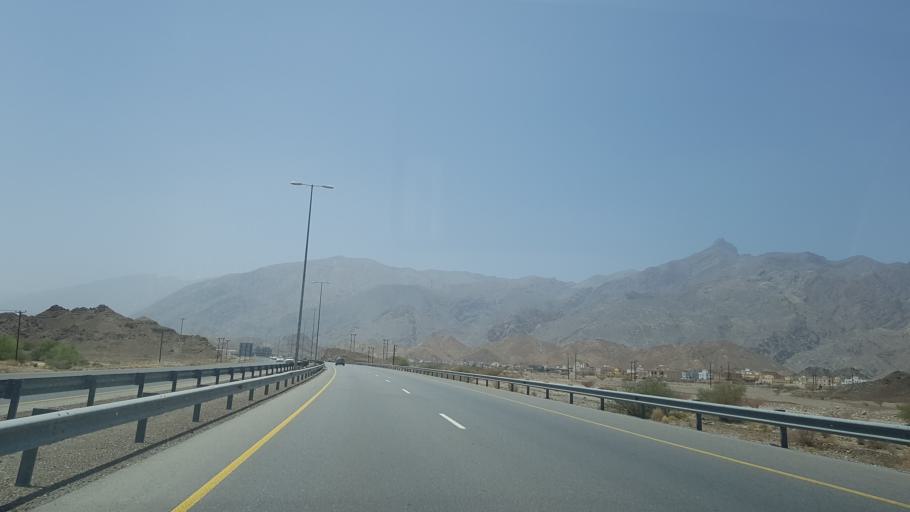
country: OM
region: Muhafazat ad Dakhiliyah
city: Sufalat Sama'il
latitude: 23.3257
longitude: 57.9671
